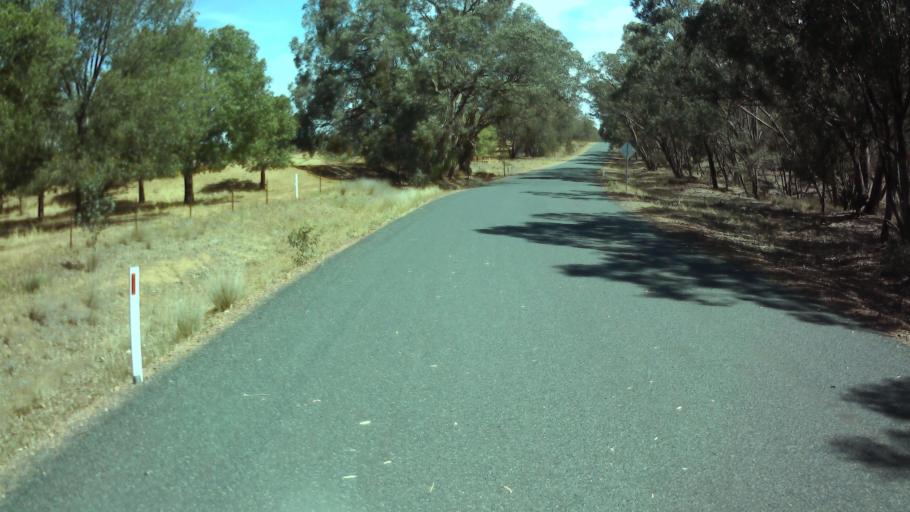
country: AU
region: New South Wales
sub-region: Weddin
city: Grenfell
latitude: -34.0020
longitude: 148.1308
